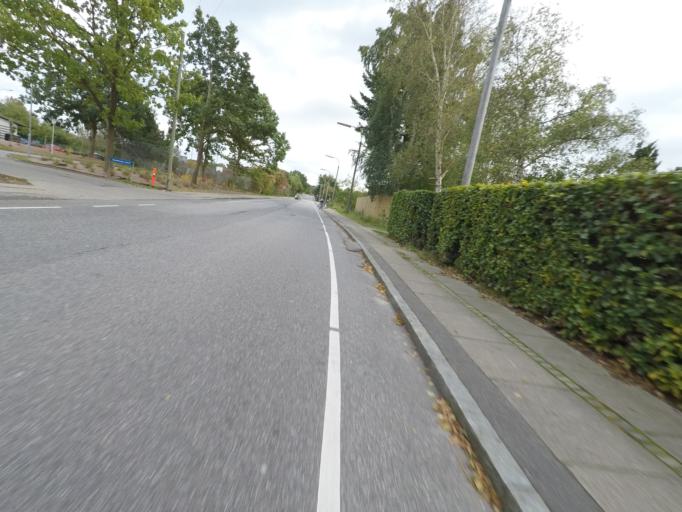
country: DK
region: Capital Region
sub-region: Ballerup Kommune
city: Ballerup
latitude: 55.7513
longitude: 12.3932
